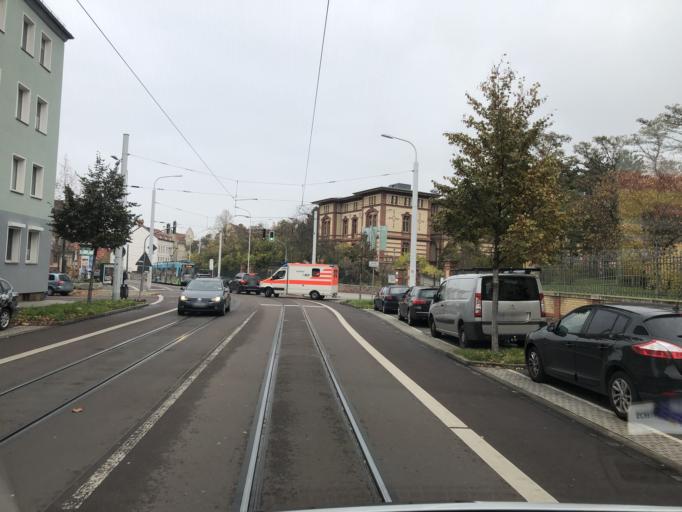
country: DE
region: Saxony-Anhalt
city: Halle (Saale)
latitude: 51.4697
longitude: 11.9693
